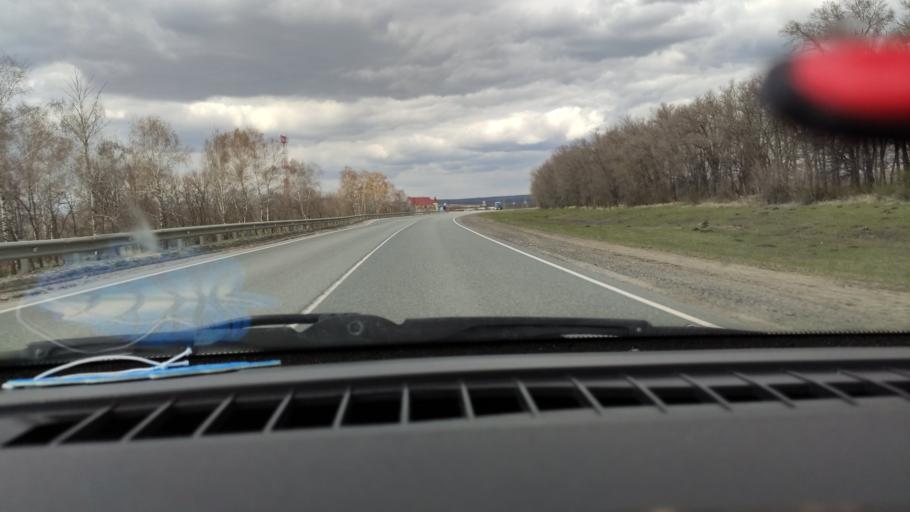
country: RU
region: Saratov
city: Tersa
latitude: 52.0845
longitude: 47.5540
